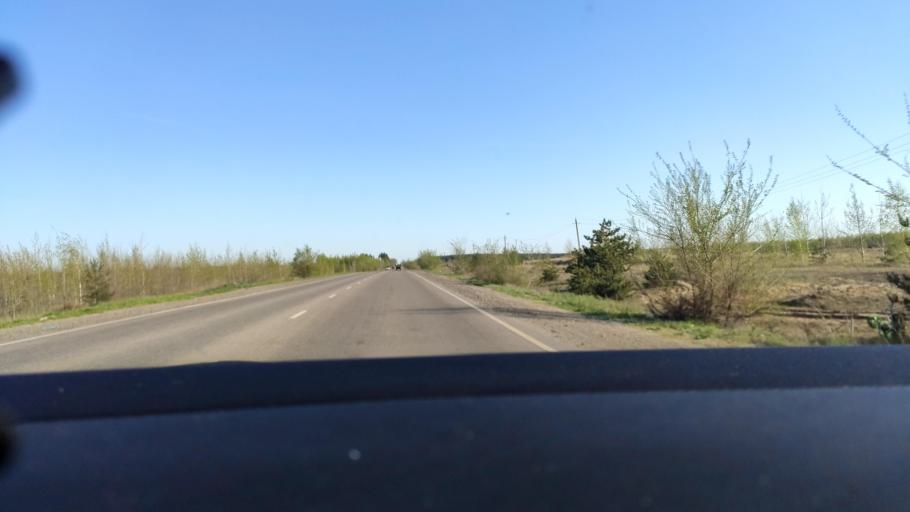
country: RU
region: Voronezj
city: Maslovka
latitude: 51.5763
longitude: 39.2670
